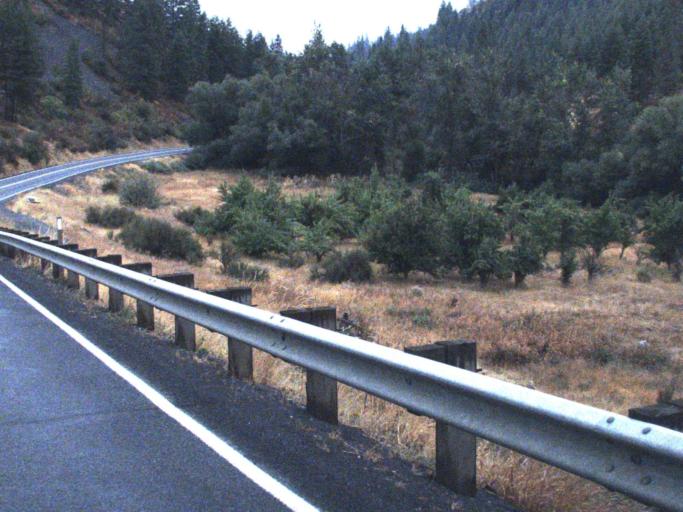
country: US
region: Washington
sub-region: Lincoln County
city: Davenport
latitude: 47.7706
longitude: -117.8925
